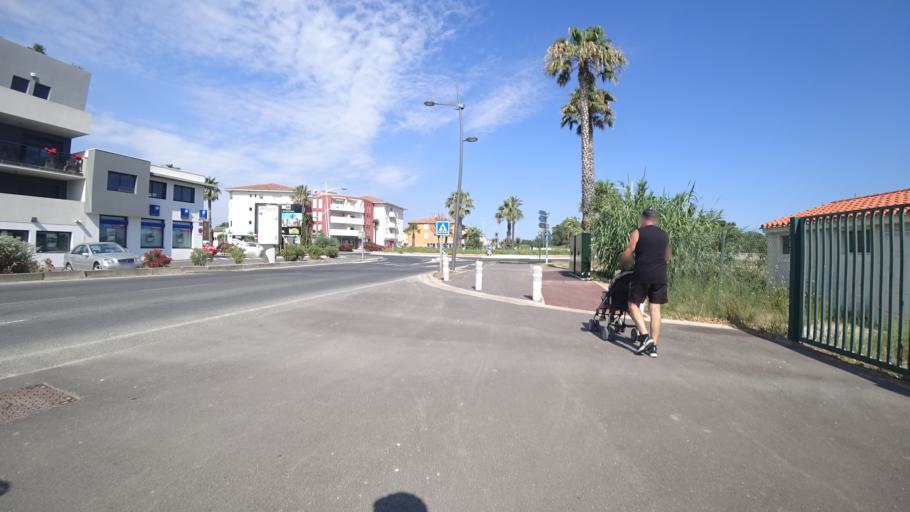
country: FR
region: Languedoc-Roussillon
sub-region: Departement des Pyrenees-Orientales
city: Canet-en-Roussillon
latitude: 42.7032
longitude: 3.0234
